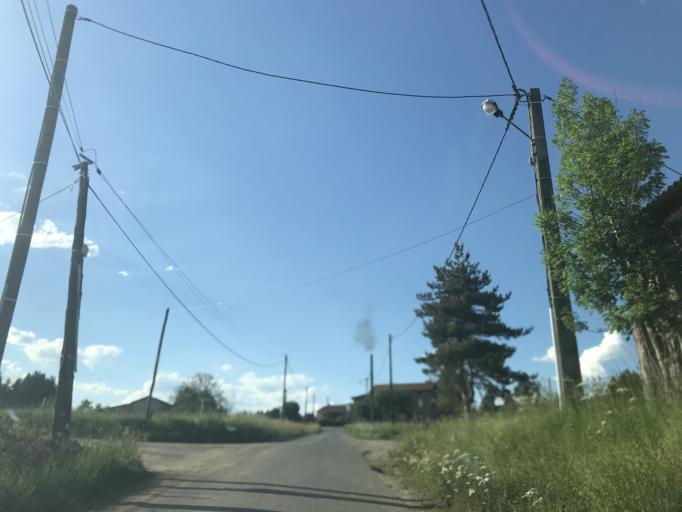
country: FR
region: Auvergne
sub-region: Departement du Puy-de-Dome
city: Job
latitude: 45.6613
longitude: 3.6771
